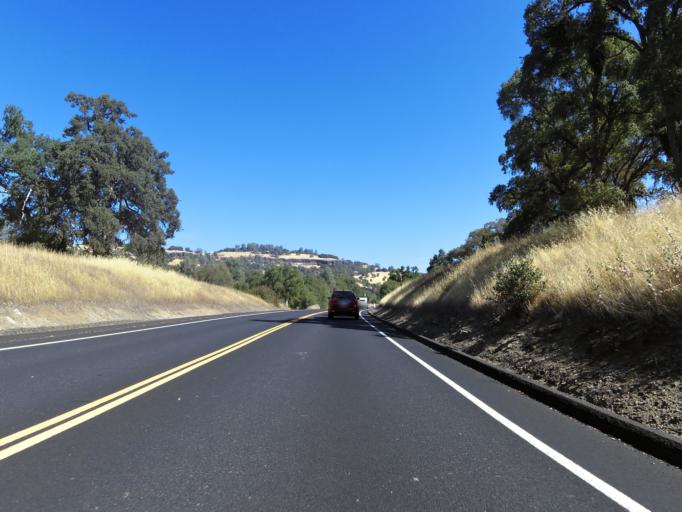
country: US
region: California
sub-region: Calaveras County
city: Murphys
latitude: 38.0976
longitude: -120.4712
